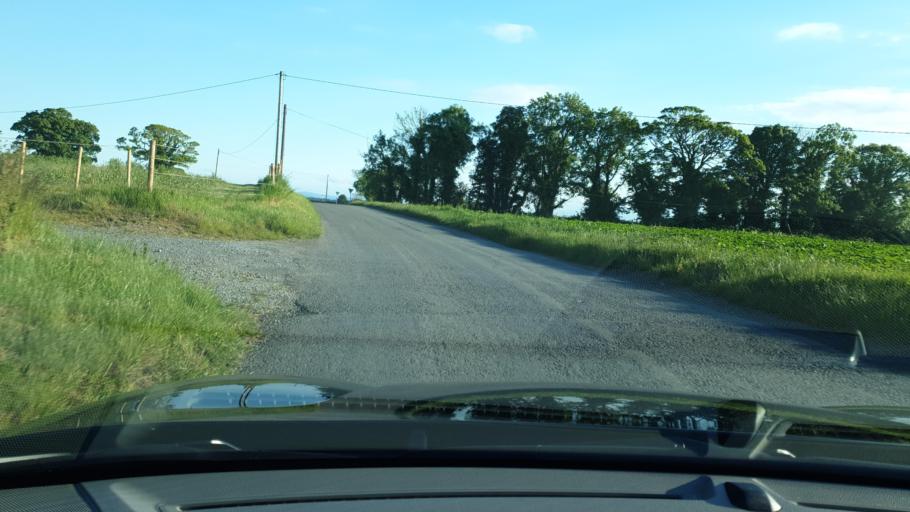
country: IE
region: Leinster
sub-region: Fingal County
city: Swords
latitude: 53.5045
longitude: -6.2401
